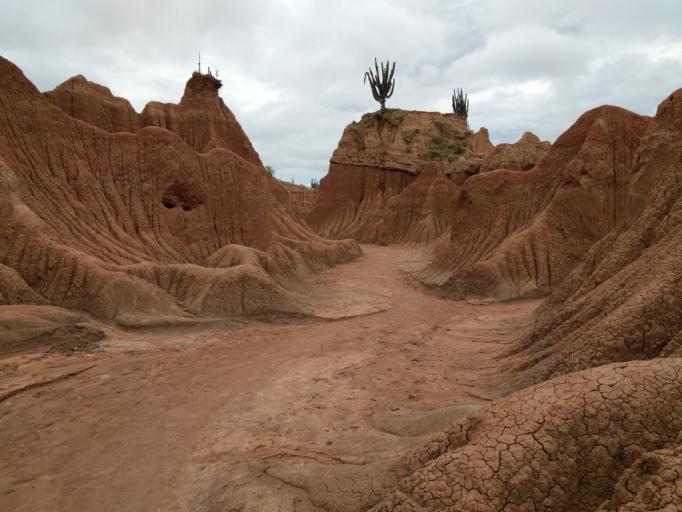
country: CO
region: Huila
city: Villavieja
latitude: 3.2327
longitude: -75.1691
